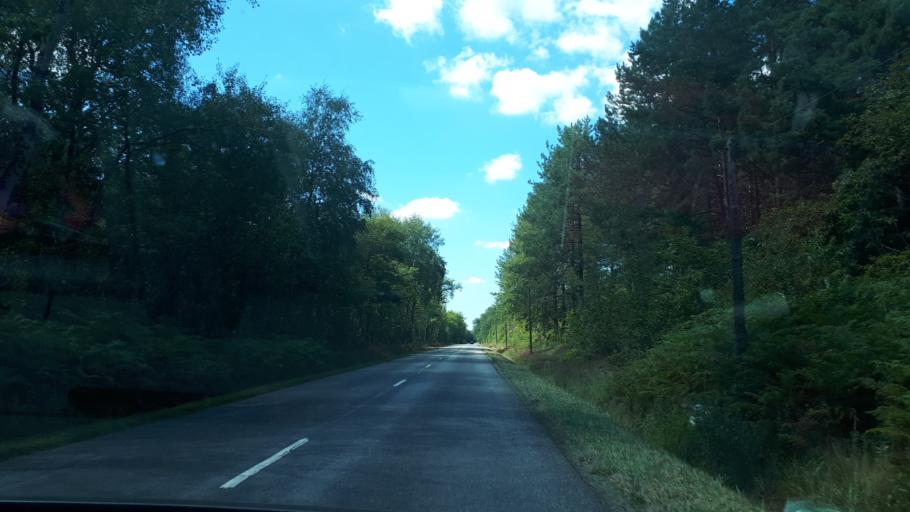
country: FR
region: Centre
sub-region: Departement du Loir-et-Cher
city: Chaumont-sur-Tharonne
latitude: 47.5694
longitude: 1.9155
